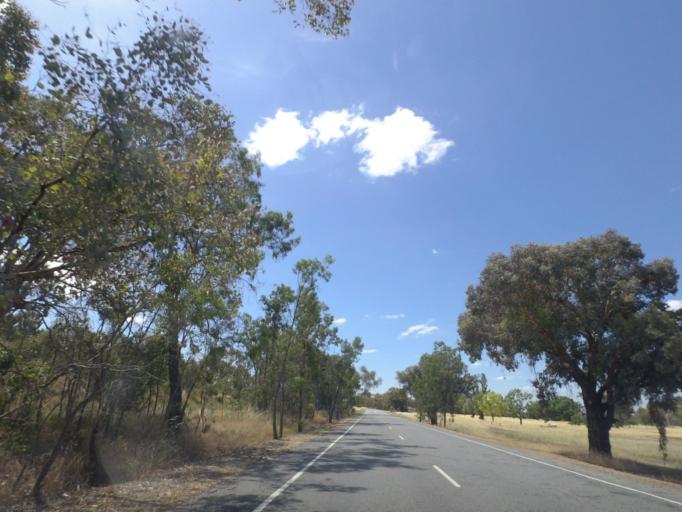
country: AU
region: Victoria
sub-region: Wangaratta
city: Wangaratta
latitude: -36.4532
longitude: 146.2376
